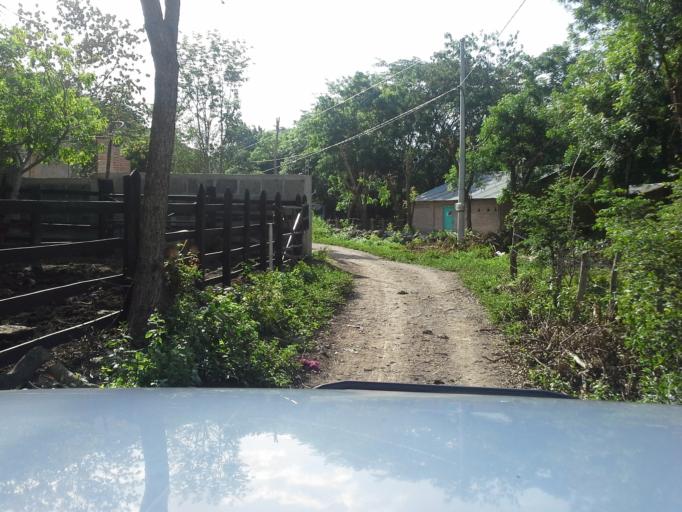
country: NI
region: Matagalpa
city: Ciudad Dario
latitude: 12.6699
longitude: -86.0492
